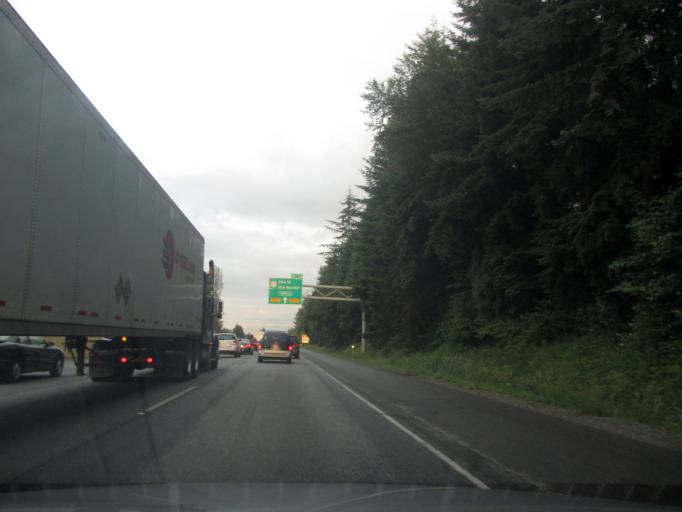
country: CA
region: British Columbia
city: Aldergrove
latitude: 49.1084
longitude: -122.5110
